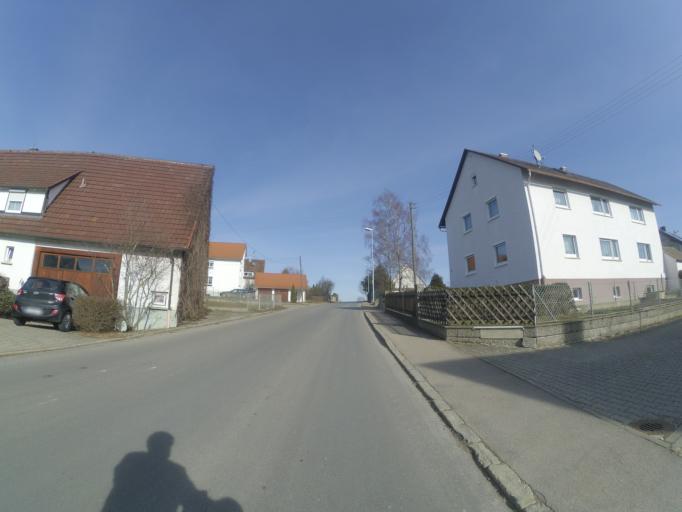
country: DE
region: Baden-Wuerttemberg
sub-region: Tuebingen Region
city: Bernstadt
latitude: 48.4863
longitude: 10.0325
